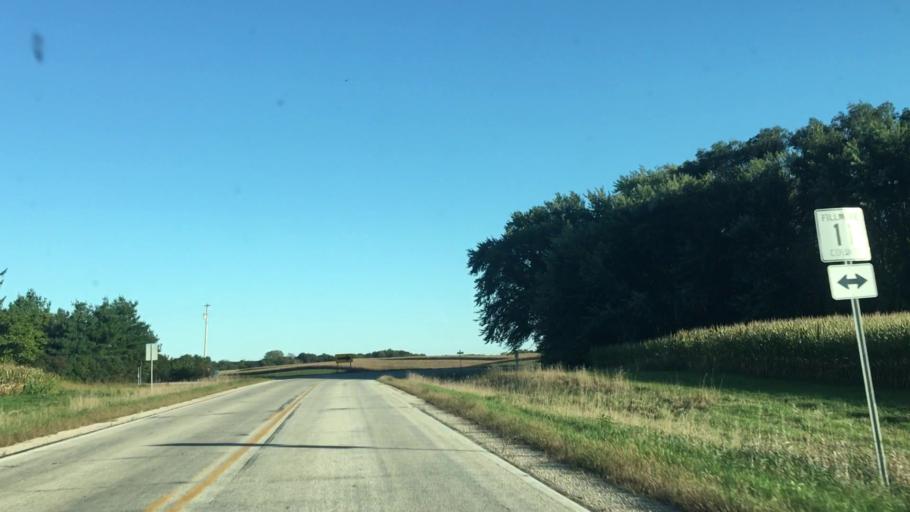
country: US
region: Minnesota
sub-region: Fillmore County
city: Chatfield
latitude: 43.8357
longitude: -92.0704
